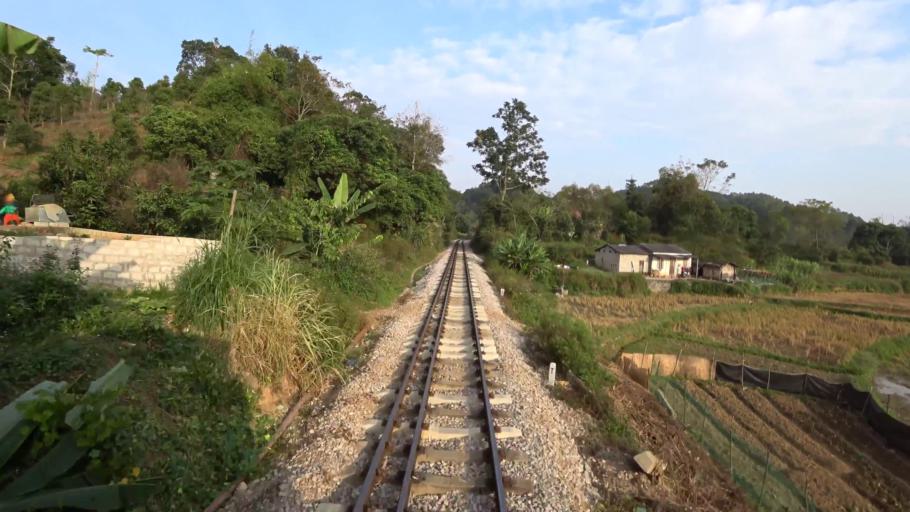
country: VN
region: Lang Son
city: Thi Tran Cao Loc
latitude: 21.9267
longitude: 106.7059
